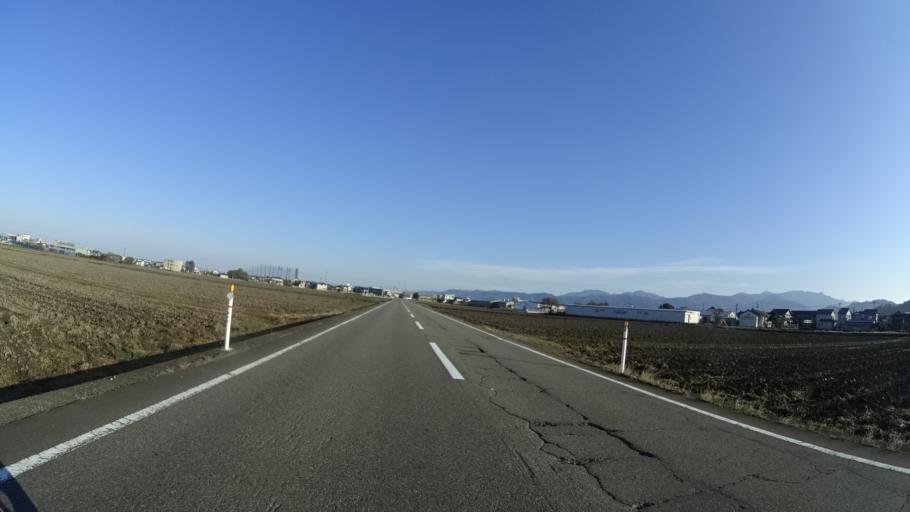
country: JP
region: Fukui
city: Fukui-shi
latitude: 36.0764
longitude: 136.2581
